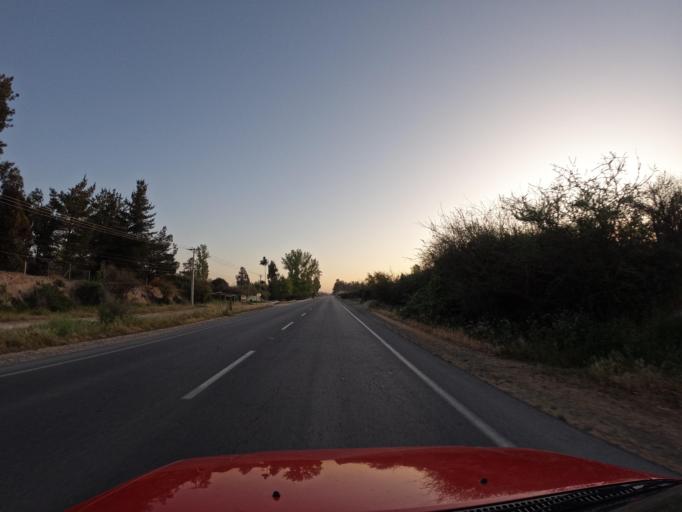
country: CL
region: O'Higgins
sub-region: Provincia de Cachapoal
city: San Vicente
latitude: -34.1538
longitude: -71.3865
